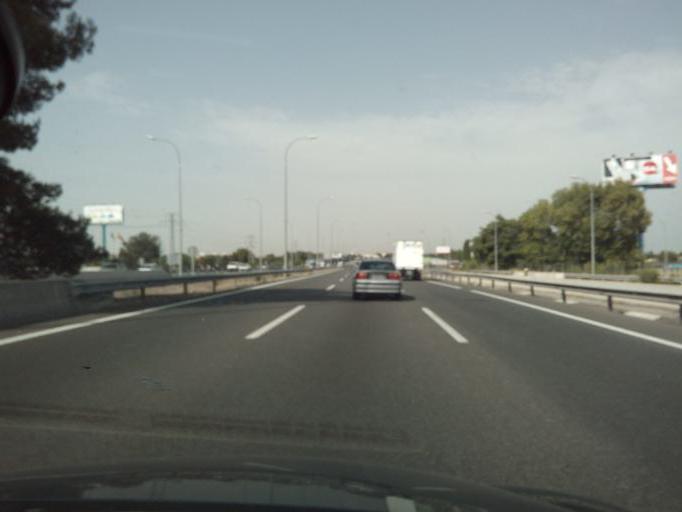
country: ES
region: Madrid
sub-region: Provincia de Madrid
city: San Fernando de Henares
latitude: 40.4497
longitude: -3.5226
